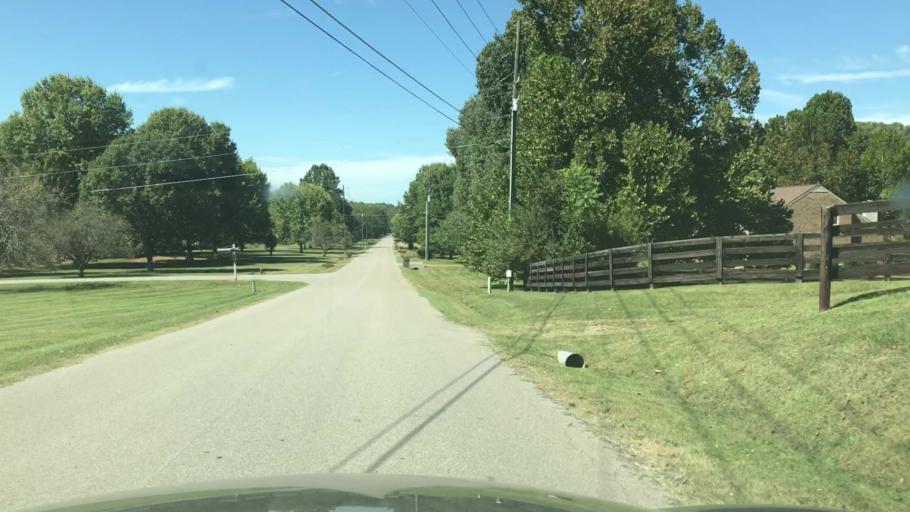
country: US
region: Tennessee
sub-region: Davidson County
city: Forest Hills
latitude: 35.9967
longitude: -86.8505
